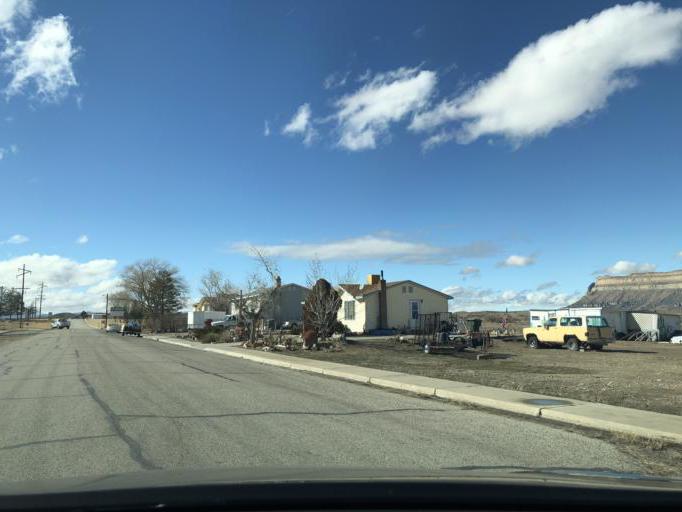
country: US
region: Utah
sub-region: Carbon County
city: East Carbon City
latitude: 39.0006
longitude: -110.1701
